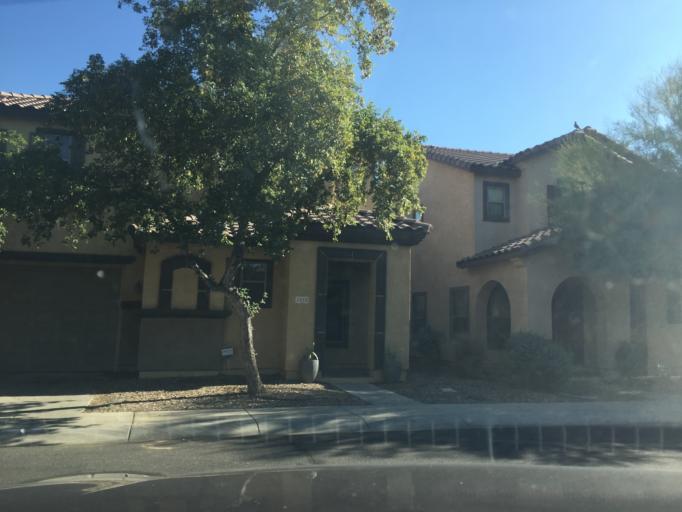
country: US
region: Arizona
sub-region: Maricopa County
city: Tolleson
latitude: 33.4640
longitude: -112.2307
